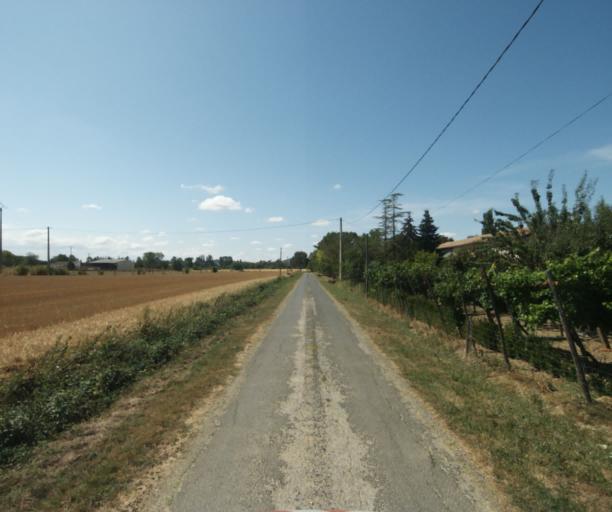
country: FR
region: Midi-Pyrenees
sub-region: Departement de la Haute-Garonne
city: Revel
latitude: 43.4884
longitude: 1.9935
